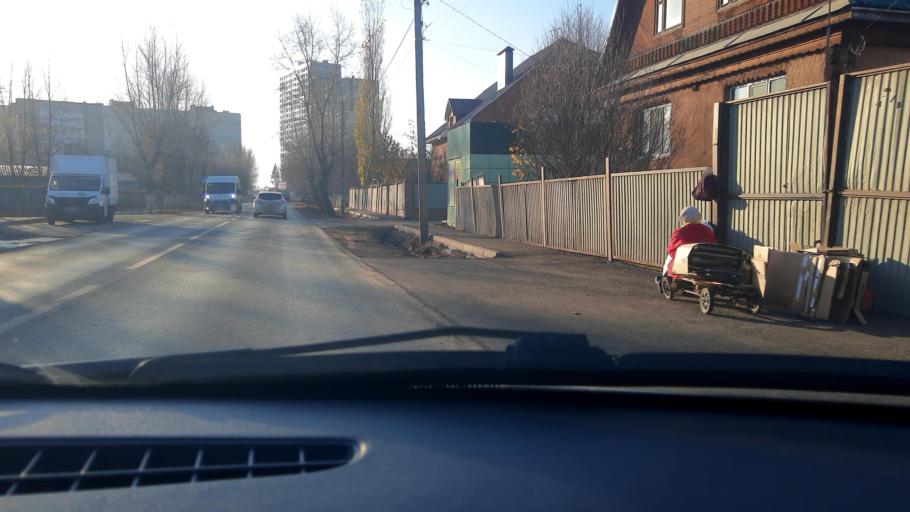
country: RU
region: Bashkortostan
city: Avdon
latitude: 54.6997
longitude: 55.8235
